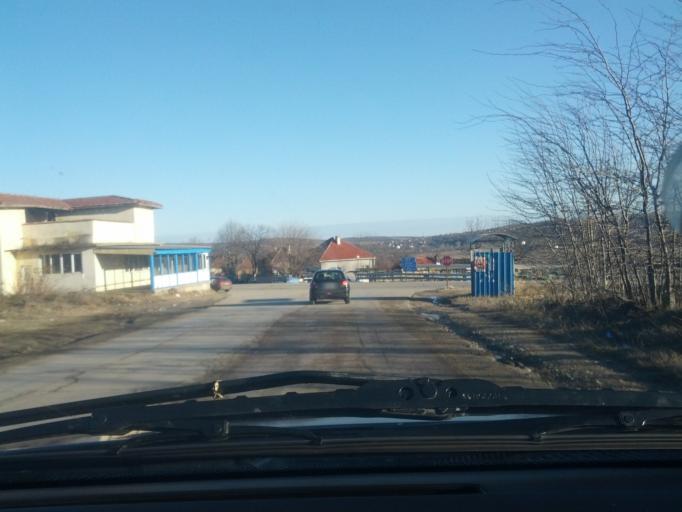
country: BG
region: Vratsa
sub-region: Obshtina Miziya
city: Miziya
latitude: 43.6254
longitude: 23.8274
